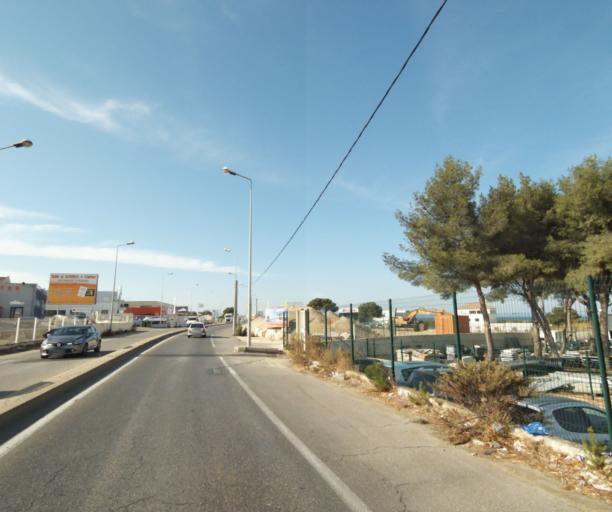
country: FR
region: Provence-Alpes-Cote d'Azur
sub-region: Departement des Bouches-du-Rhone
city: Chateauneuf-les-Martigues
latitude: 43.3936
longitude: 5.1406
